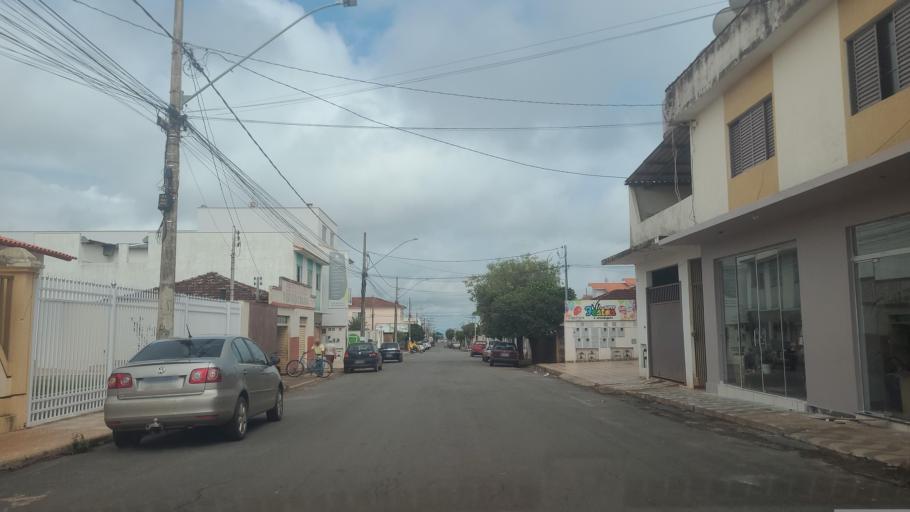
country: BR
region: Minas Gerais
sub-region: Carmo Do Paranaiba
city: Carmo do Paranaiba
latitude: -19.1938
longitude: -46.2439
